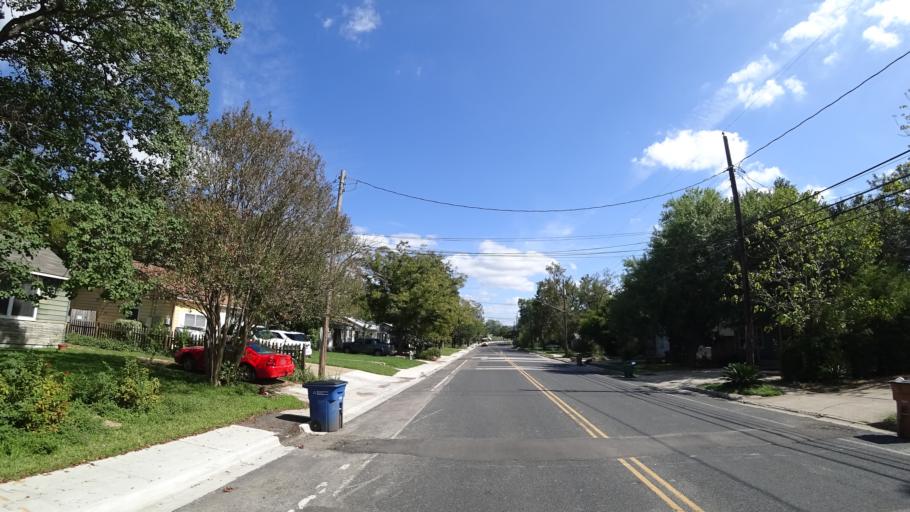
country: US
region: Texas
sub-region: Travis County
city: Austin
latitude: 30.3398
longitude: -97.7249
